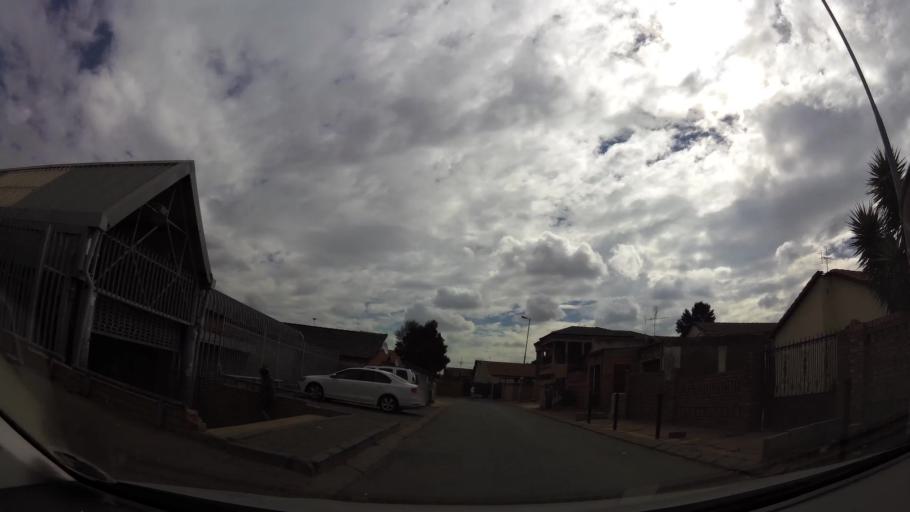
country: ZA
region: Gauteng
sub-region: City of Johannesburg Metropolitan Municipality
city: Soweto
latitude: -26.2831
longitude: 27.8549
